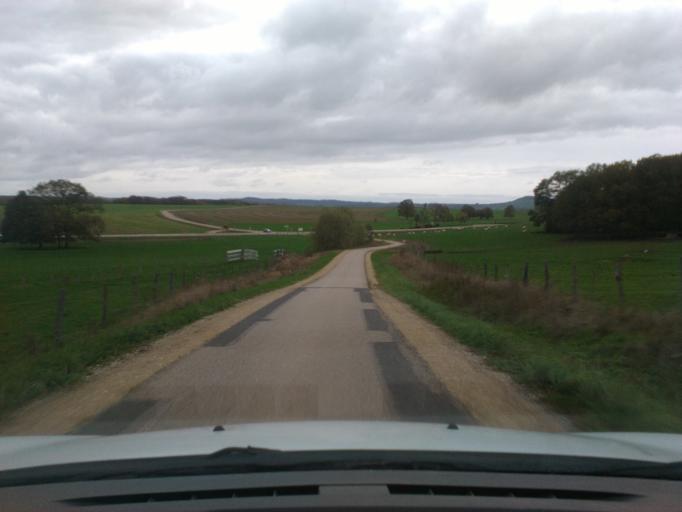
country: FR
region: Lorraine
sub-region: Departement des Vosges
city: Mirecourt
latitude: 48.3382
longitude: 6.1207
